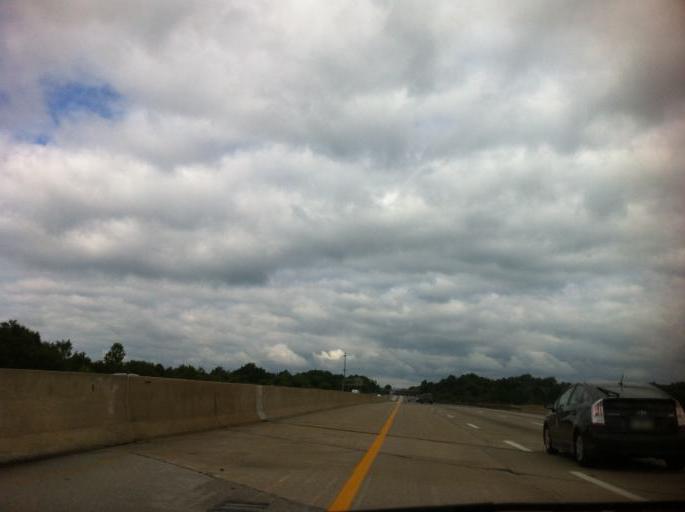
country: US
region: Ohio
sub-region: Trumbull County
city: Newton Falls
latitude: 41.2281
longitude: -80.9684
